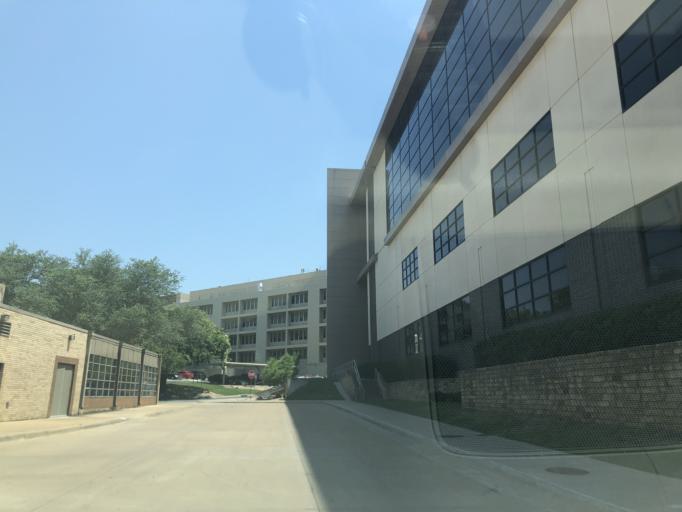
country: US
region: Texas
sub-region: Dallas County
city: Dallas
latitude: 32.8104
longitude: -96.8415
